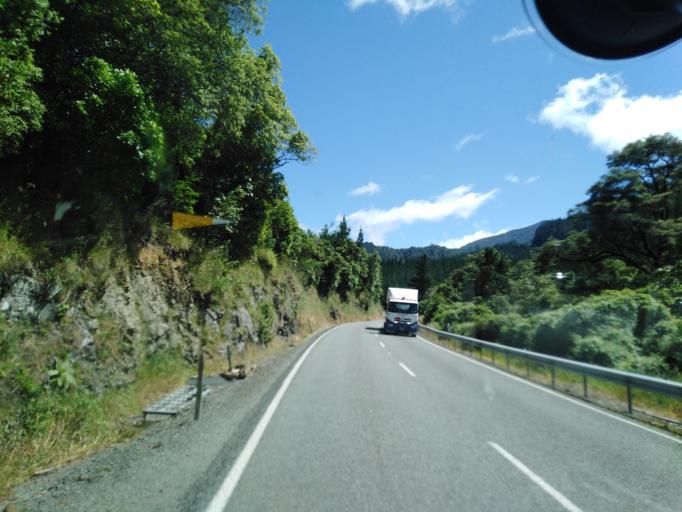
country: NZ
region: Nelson
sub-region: Nelson City
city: Nelson
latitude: -41.1736
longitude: 173.5629
